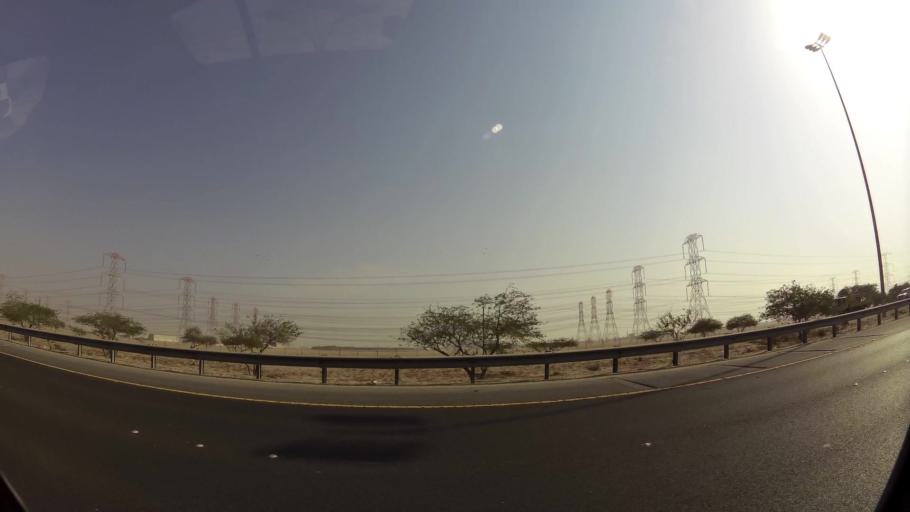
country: KW
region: Al Ahmadi
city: Al Ahmadi
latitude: 28.9815
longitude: 48.1075
